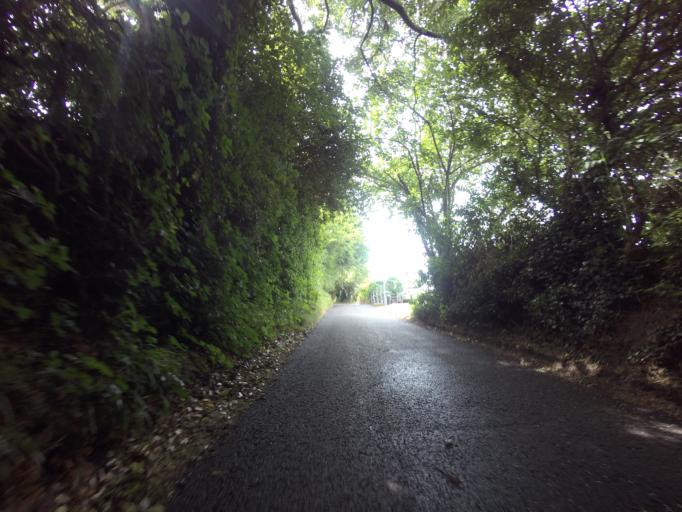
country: GB
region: England
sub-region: Kent
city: Halstead
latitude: 51.3516
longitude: 0.1401
